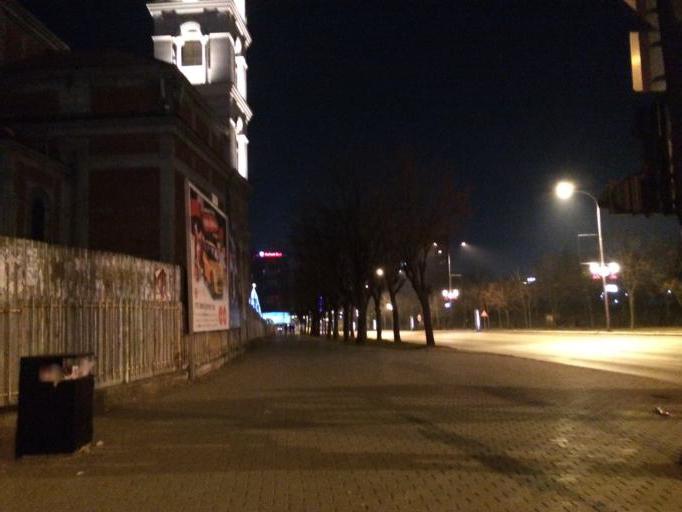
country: XK
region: Pristina
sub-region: Komuna e Prishtines
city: Pristina
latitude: 42.6557
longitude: 21.1595
